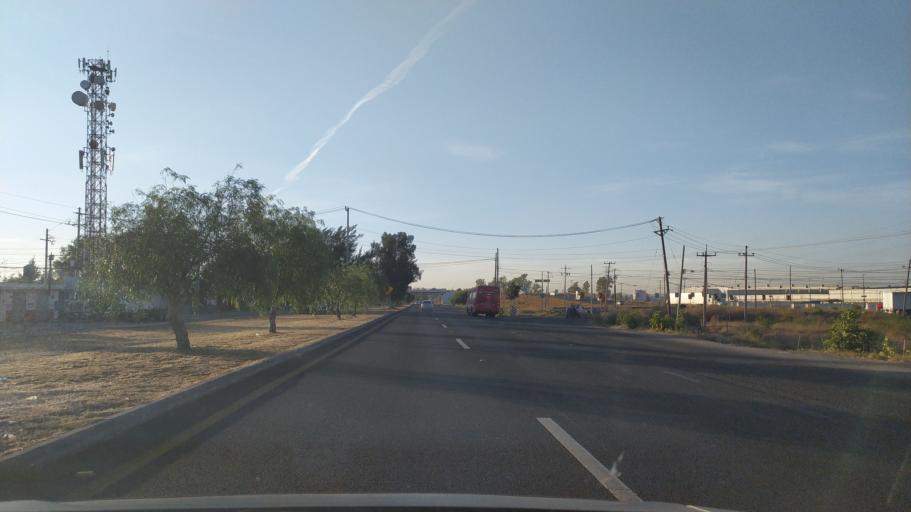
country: MX
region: Jalisco
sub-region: Tlajomulco de Zuniga
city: Rancho Alegre [Fraccionamiento]
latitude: 20.4886
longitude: -103.2721
